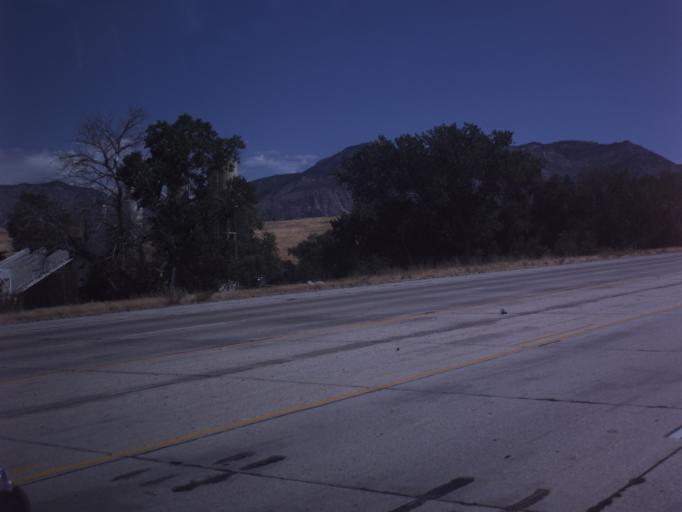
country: US
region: Utah
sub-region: Weber County
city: Ogden
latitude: 41.2295
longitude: -112.0019
